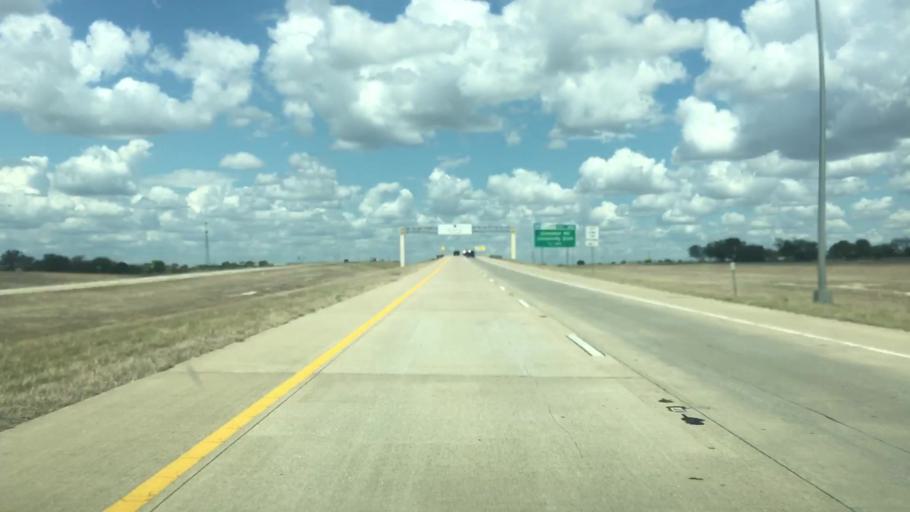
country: US
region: Texas
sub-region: Williamson County
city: Hutto
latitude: 30.5702
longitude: -97.5822
